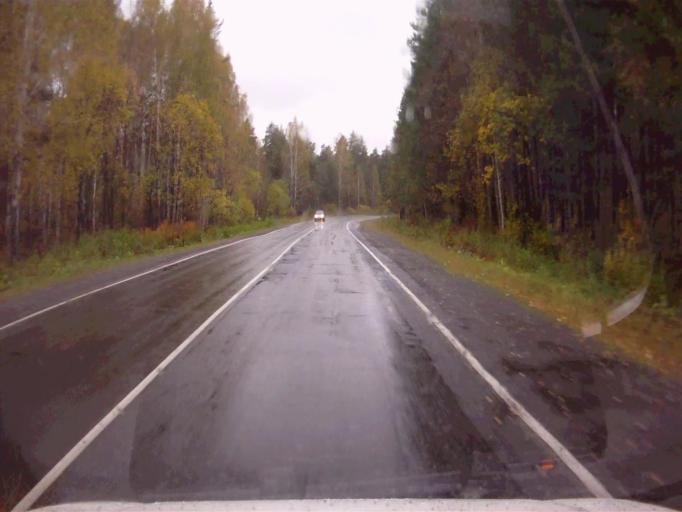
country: RU
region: Chelyabinsk
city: Verkhniy Ufaley
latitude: 55.9592
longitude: 60.3853
